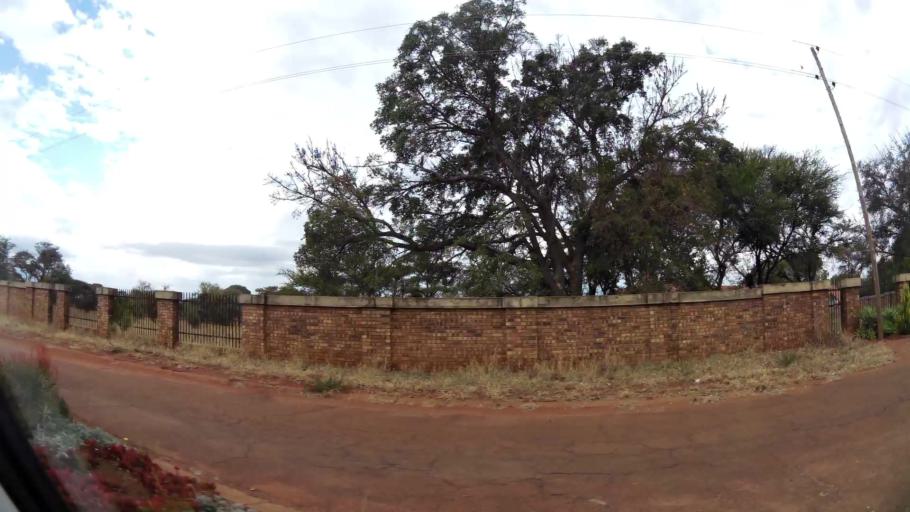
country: ZA
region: Limpopo
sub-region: Waterberg District Municipality
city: Modimolle
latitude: -24.5077
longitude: 28.7182
